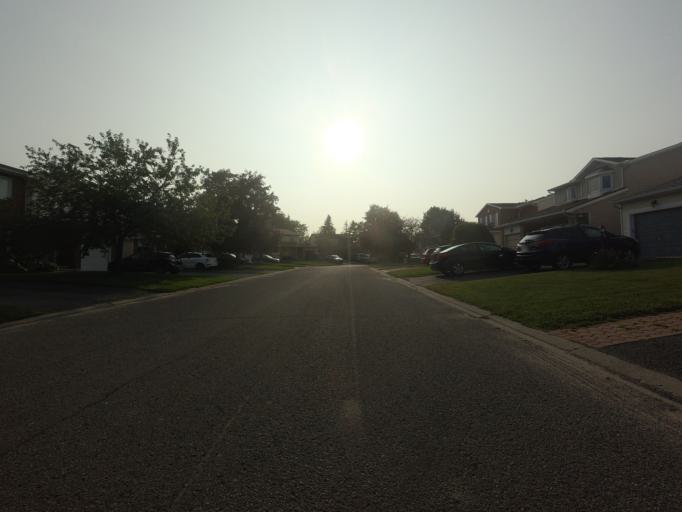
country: CA
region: Ontario
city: Bells Corners
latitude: 45.3368
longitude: -75.7601
